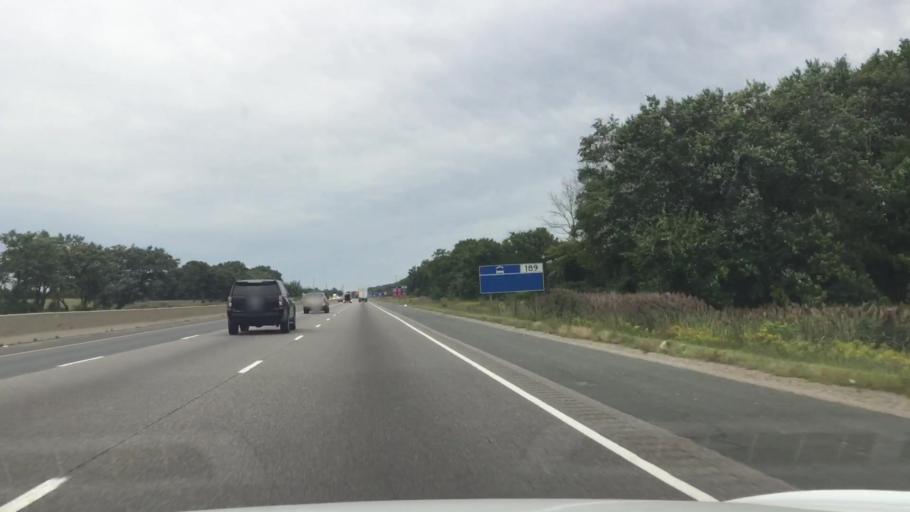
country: CA
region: Ontario
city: Dorchester
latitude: 42.9418
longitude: -81.1401
